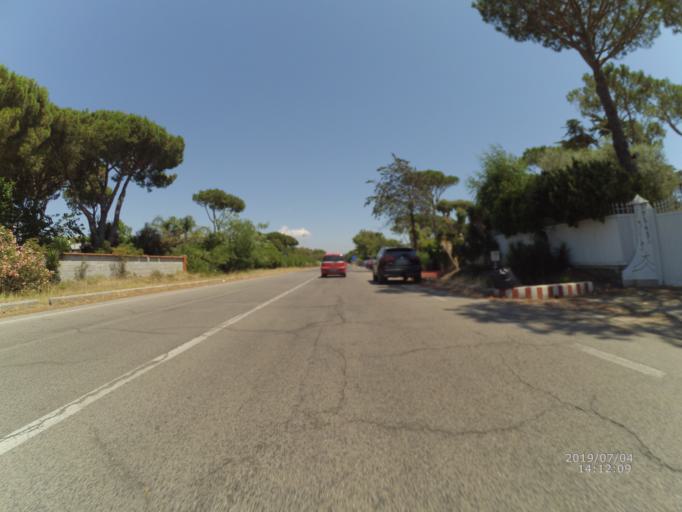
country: IT
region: Latium
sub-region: Provincia di Latina
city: Monte San Biagio
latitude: 41.2979
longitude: 13.2987
